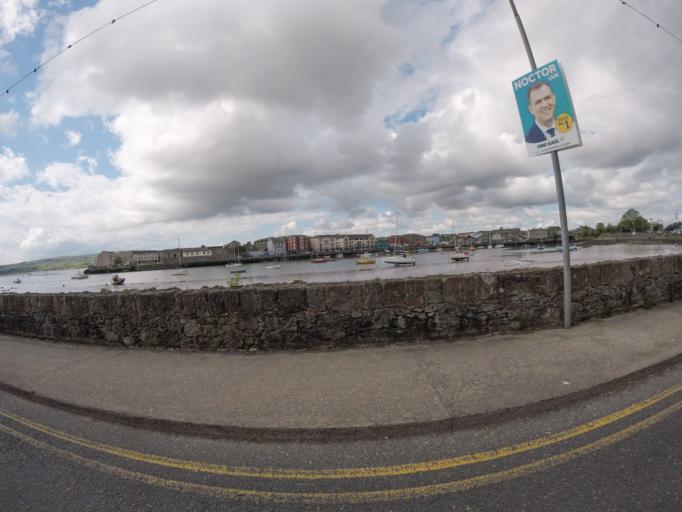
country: IE
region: Munster
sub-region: Waterford
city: Dungarvan
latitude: 52.0913
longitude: -7.6150
